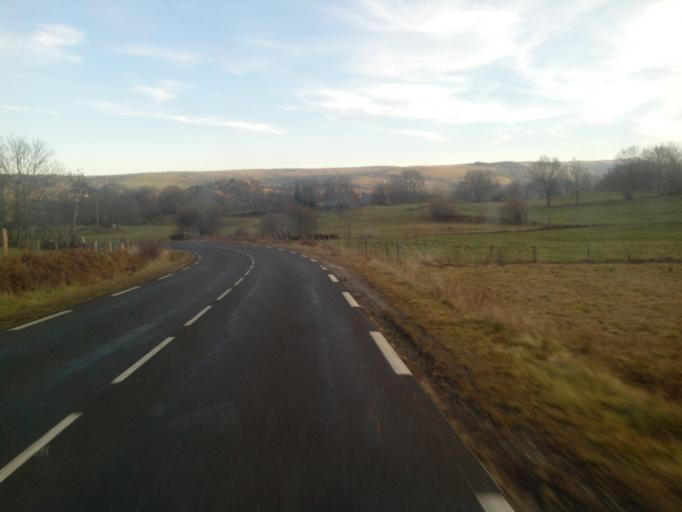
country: FR
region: Auvergne
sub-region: Departement du Cantal
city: Riom-es-Montagnes
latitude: 45.2558
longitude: 2.7014
